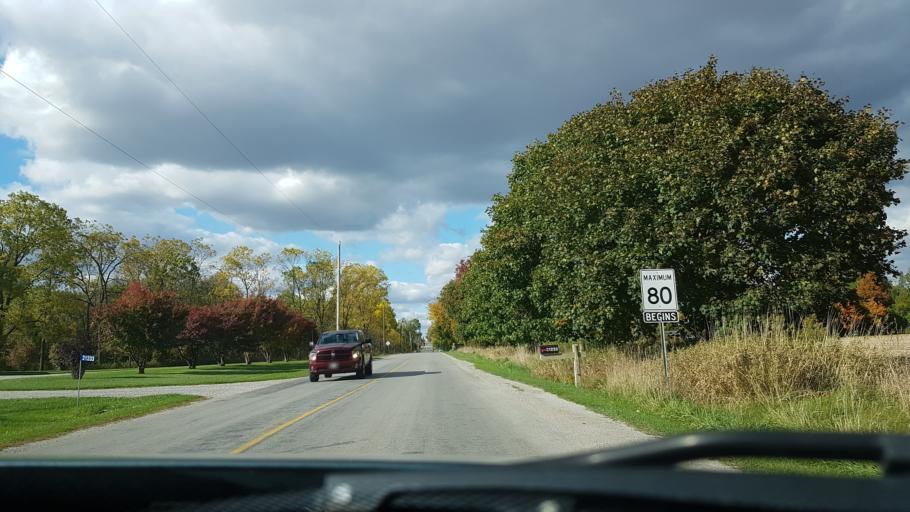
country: CA
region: Ontario
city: Delaware
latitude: 43.0031
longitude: -81.3974
